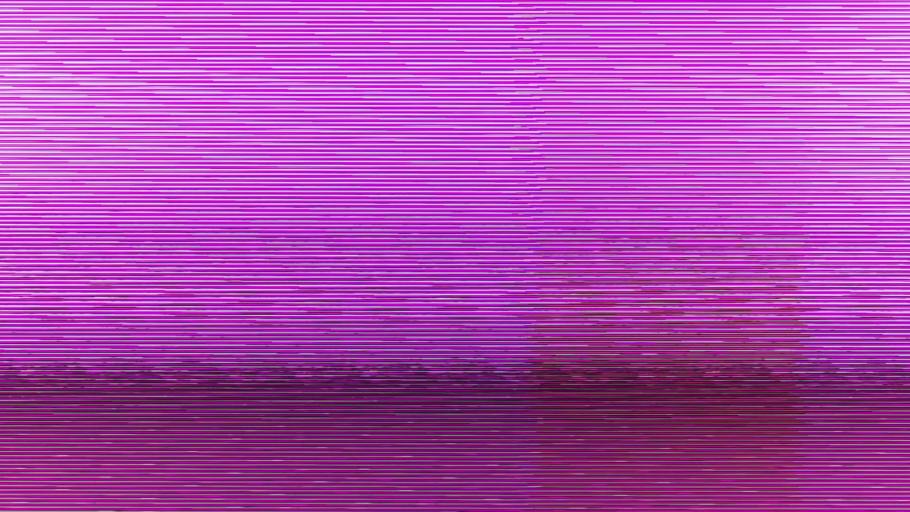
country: US
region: Michigan
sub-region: Macomb County
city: Romeo
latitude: 42.7599
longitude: -83.0109
